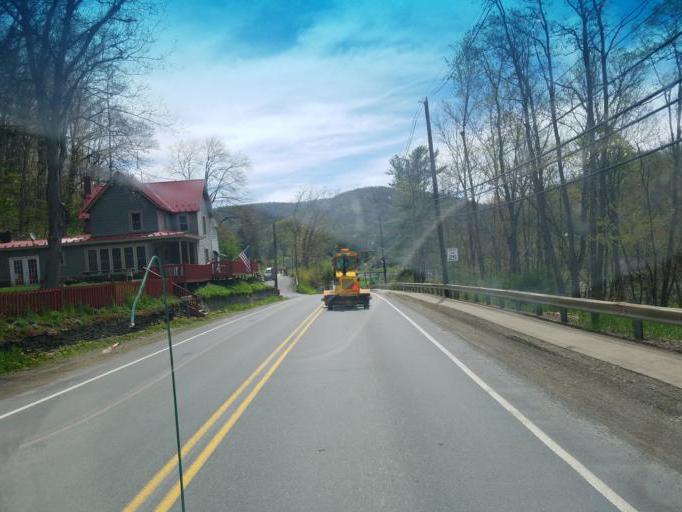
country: US
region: Pennsylvania
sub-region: Potter County
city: Galeton
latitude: 41.7367
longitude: -77.6494
